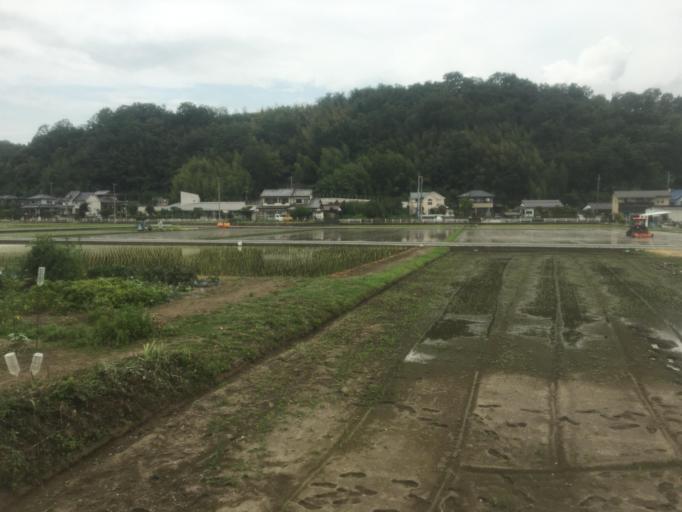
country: JP
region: Gunma
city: Fujioka
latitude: 36.2754
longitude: 139.0377
